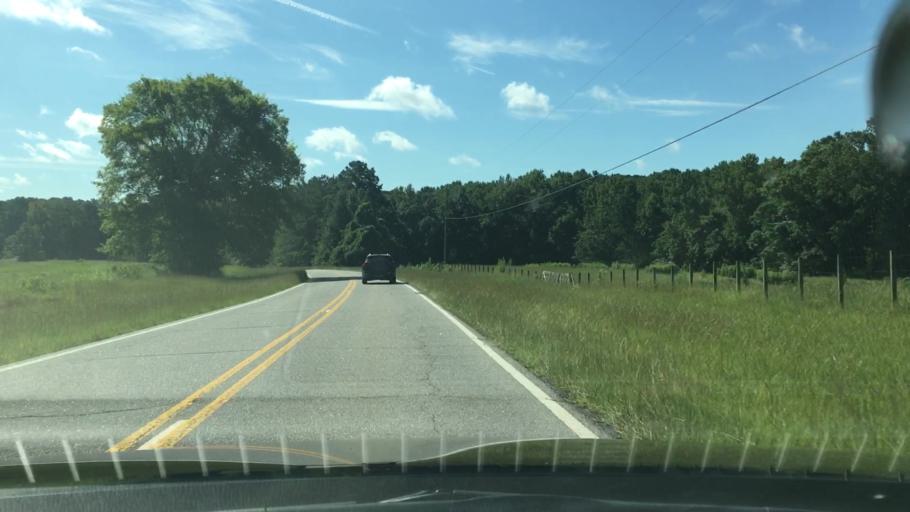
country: US
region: Georgia
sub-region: Putnam County
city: Jefferson
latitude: 33.3921
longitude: -83.2657
